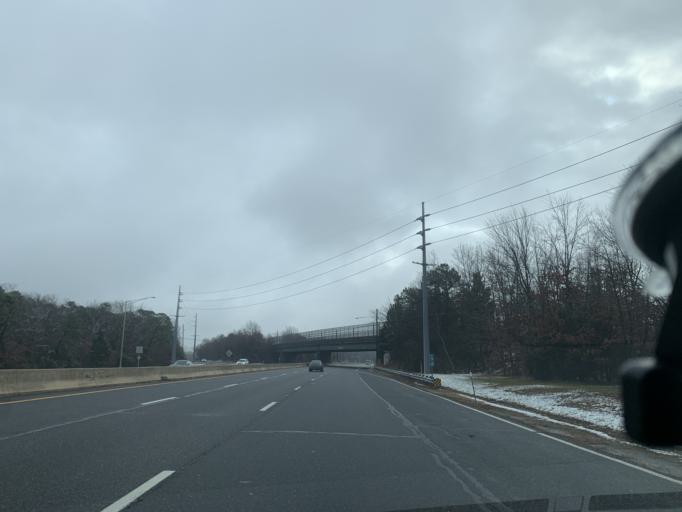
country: US
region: New Jersey
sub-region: Atlantic County
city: Pomona
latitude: 39.4348
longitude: -74.5884
